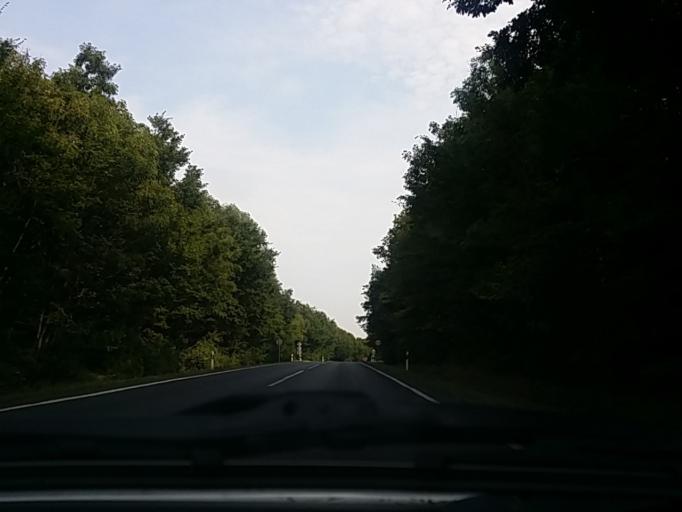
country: HU
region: Fejer
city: Szarliget
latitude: 47.5100
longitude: 18.4851
